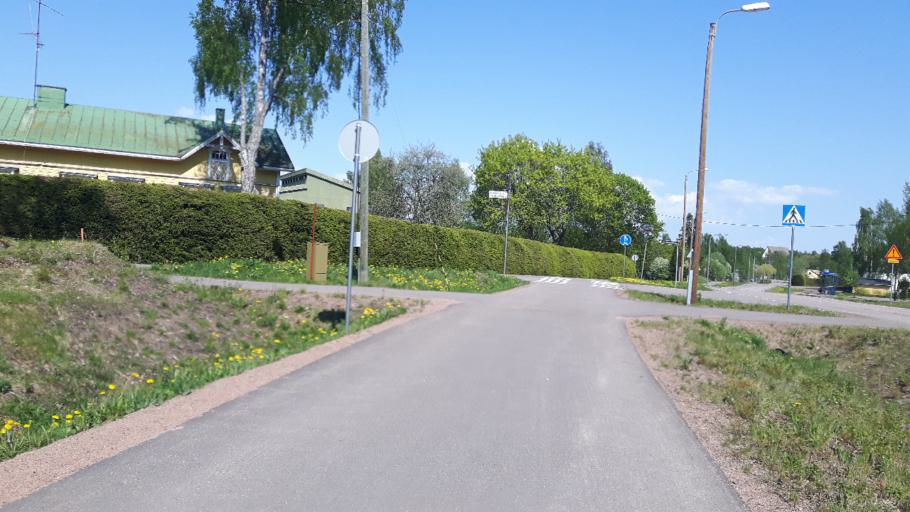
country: FI
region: Kymenlaakso
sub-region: Kotka-Hamina
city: Pyhtaeae
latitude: 60.4893
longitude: 26.5321
